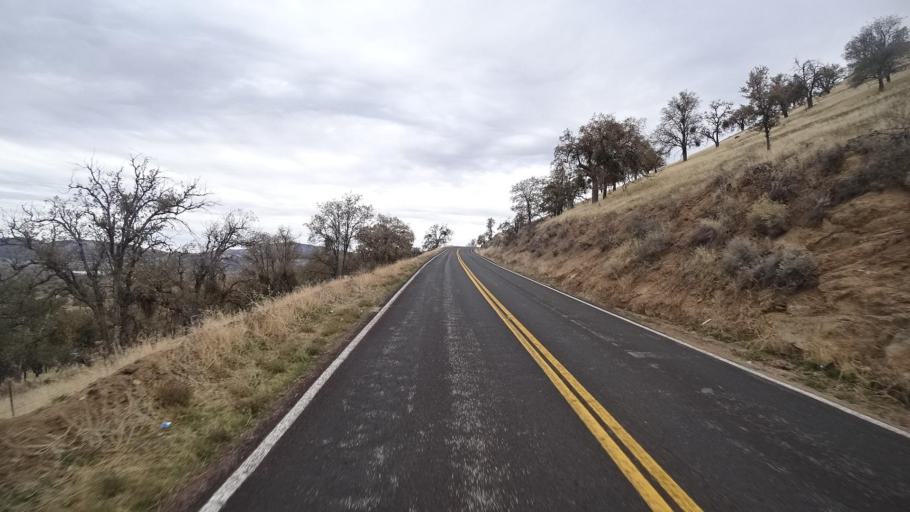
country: US
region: California
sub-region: Kern County
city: Golden Hills
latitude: 35.0920
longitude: -118.5554
